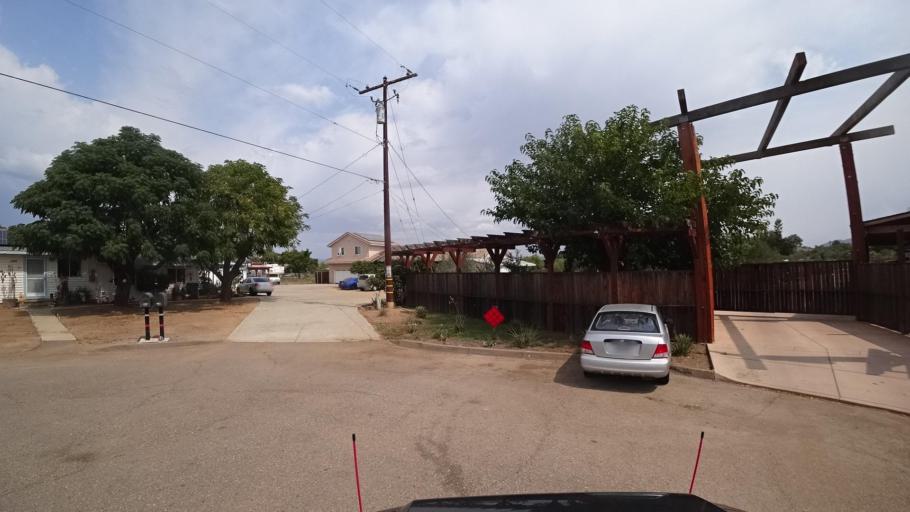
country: US
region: California
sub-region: San Diego County
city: Ramona
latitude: 33.0106
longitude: -116.9043
